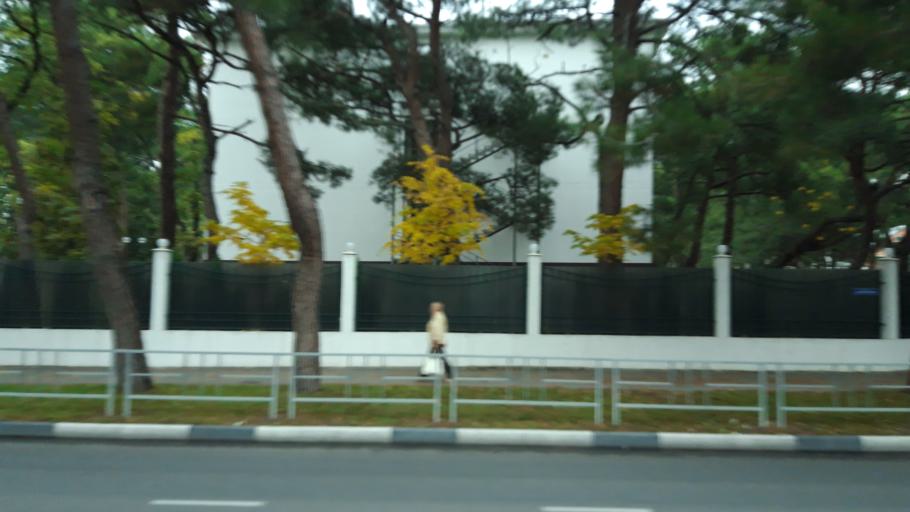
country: RU
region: Krasnodarskiy
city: Gelendzhik
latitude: 44.5707
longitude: 38.0771
